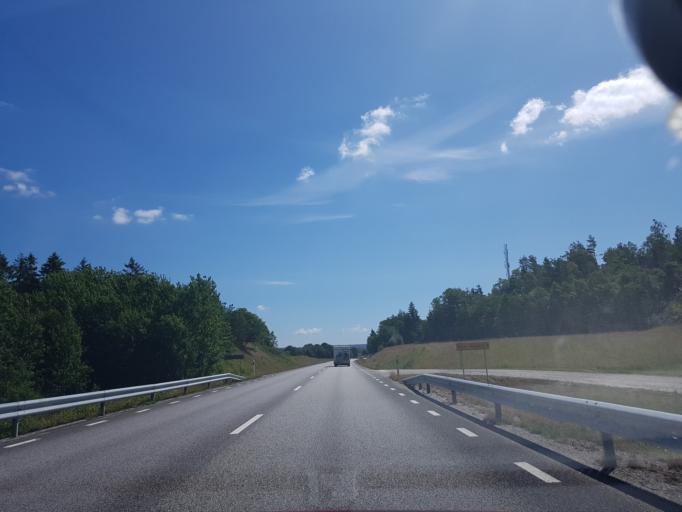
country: SE
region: Vaestra Goetaland
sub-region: Orust
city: Henan
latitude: 58.1548
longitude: 11.5594
